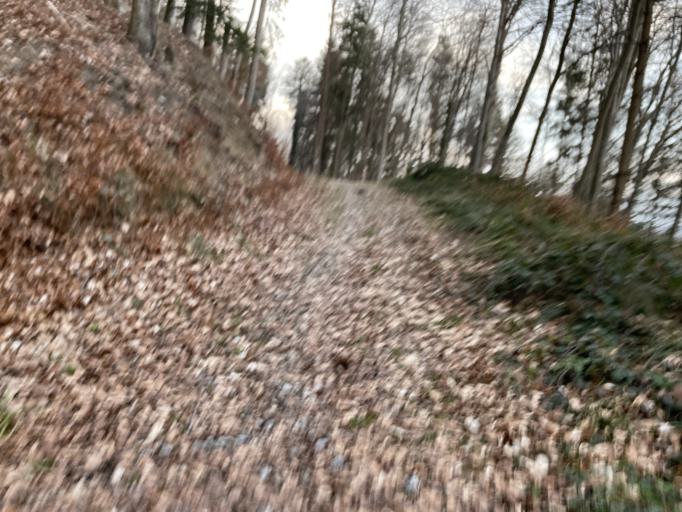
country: CH
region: Bern
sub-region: Bern-Mittelland District
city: Muhlethurnen
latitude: 46.8361
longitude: 7.5324
